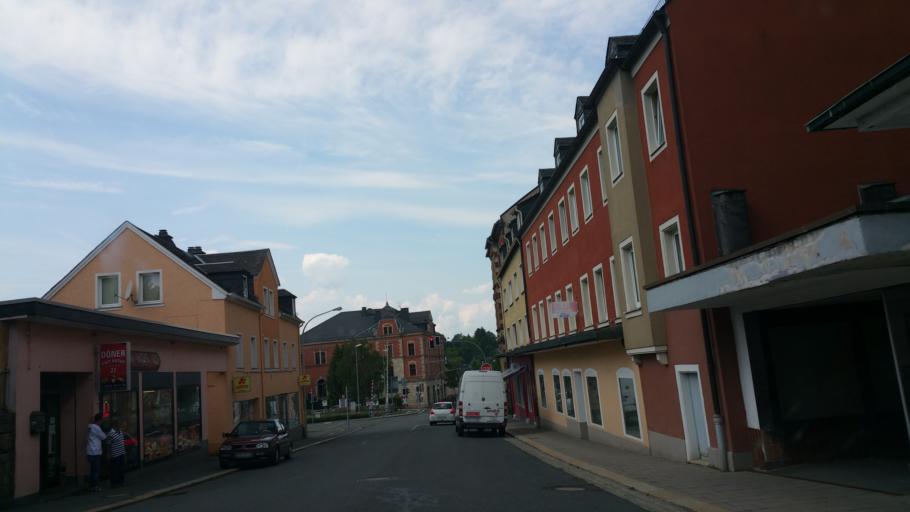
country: DE
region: Bavaria
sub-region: Upper Franconia
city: Schwarzenbach an der Saale
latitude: 50.2211
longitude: 11.9379
